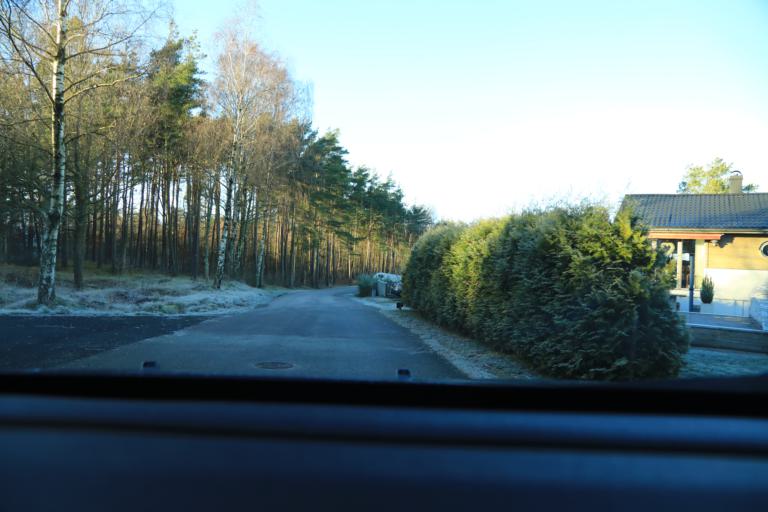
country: SE
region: Halland
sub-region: Varbergs Kommun
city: Varberg
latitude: 57.2016
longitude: 12.1902
